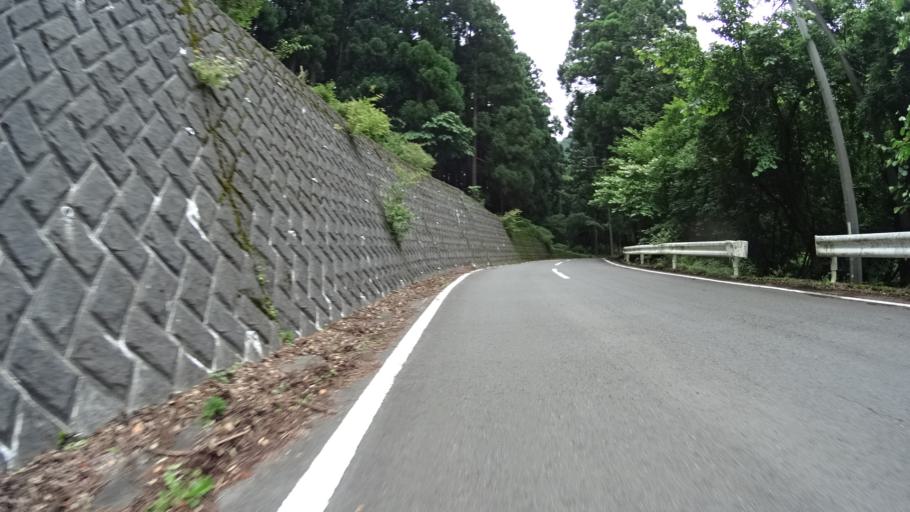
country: JP
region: Kanagawa
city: Hadano
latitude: 35.4484
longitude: 139.2129
